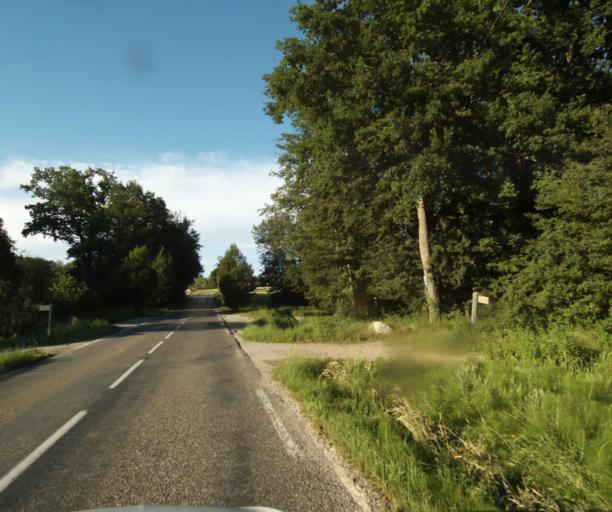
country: FR
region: Rhone-Alpes
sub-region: Departement de la Haute-Savoie
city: Messery
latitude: 46.3637
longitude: 6.3183
